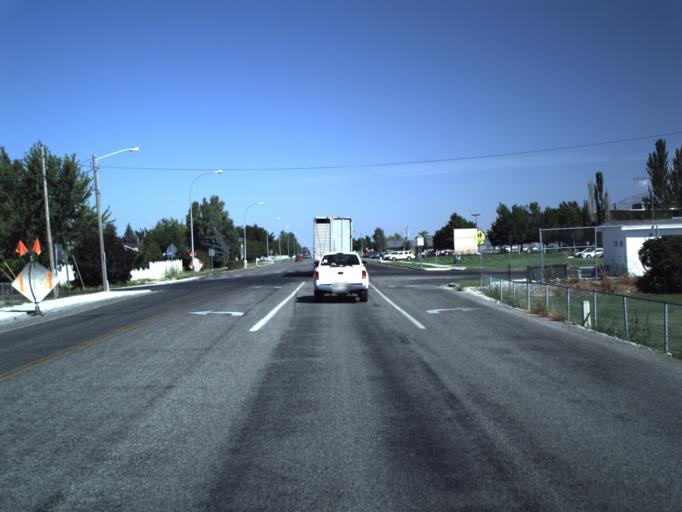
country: US
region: Utah
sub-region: Cache County
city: Hyrum
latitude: 41.6267
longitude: -111.8326
